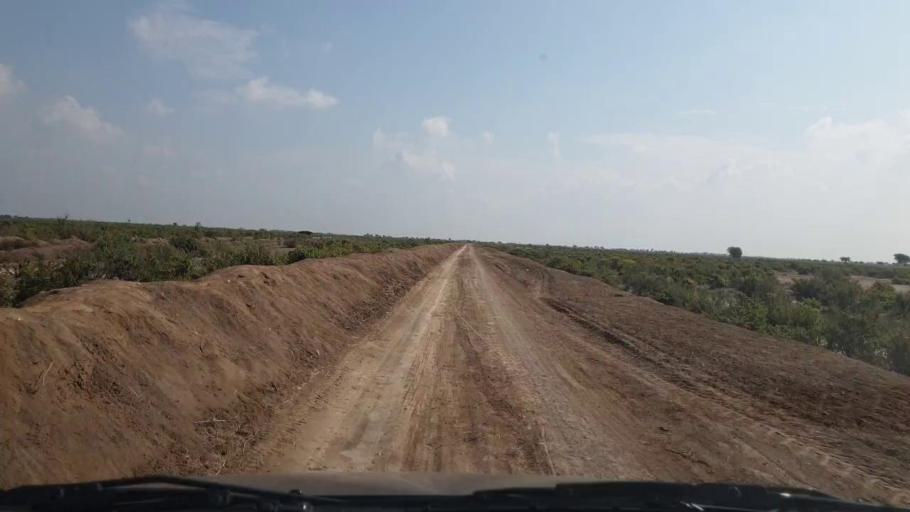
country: PK
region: Sindh
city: Badin
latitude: 24.4977
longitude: 68.6070
